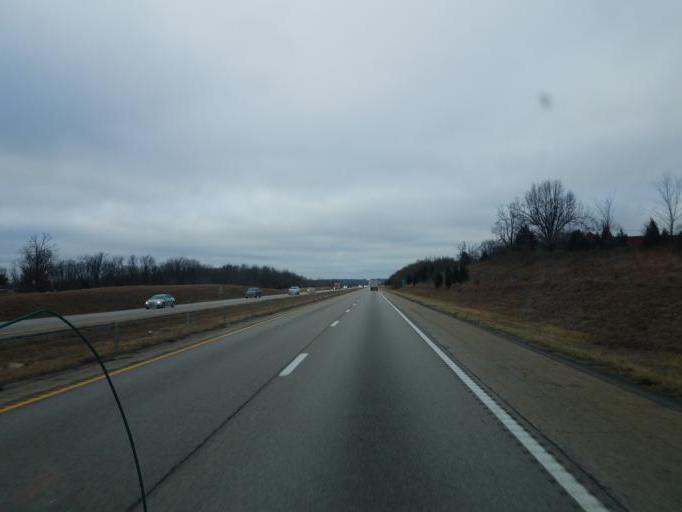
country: US
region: Missouri
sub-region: Laclede County
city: Lebanon
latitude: 37.5881
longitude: -92.7367
